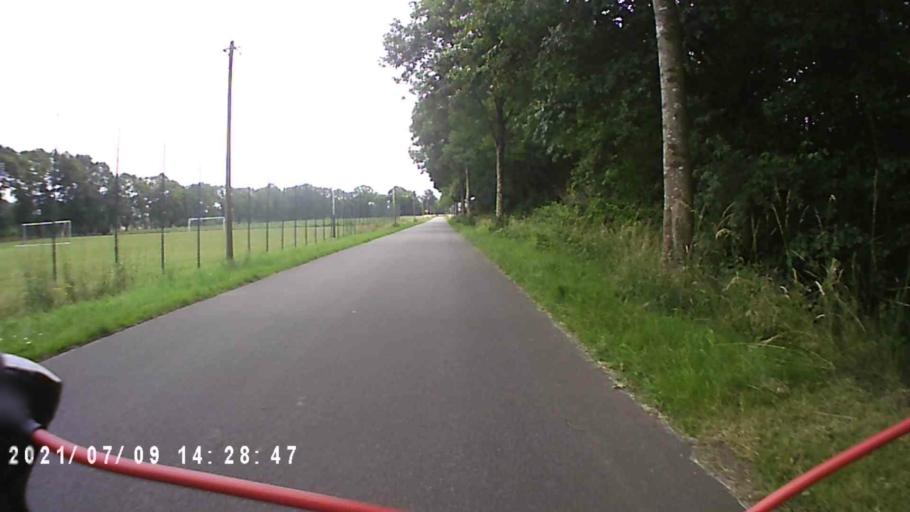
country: DE
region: Lower Saxony
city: Weener
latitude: 53.1285
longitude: 7.2990
